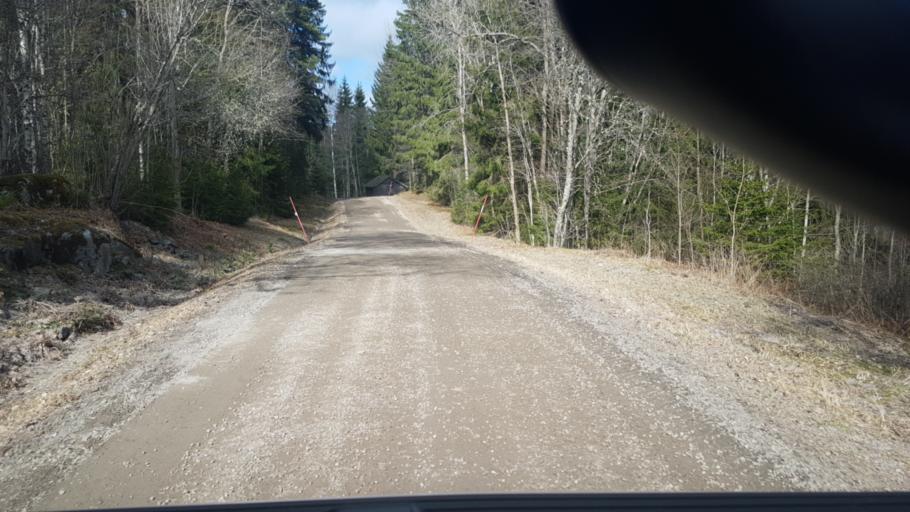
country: SE
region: Vaermland
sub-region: Eda Kommun
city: Amotfors
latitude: 59.7939
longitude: 12.4444
